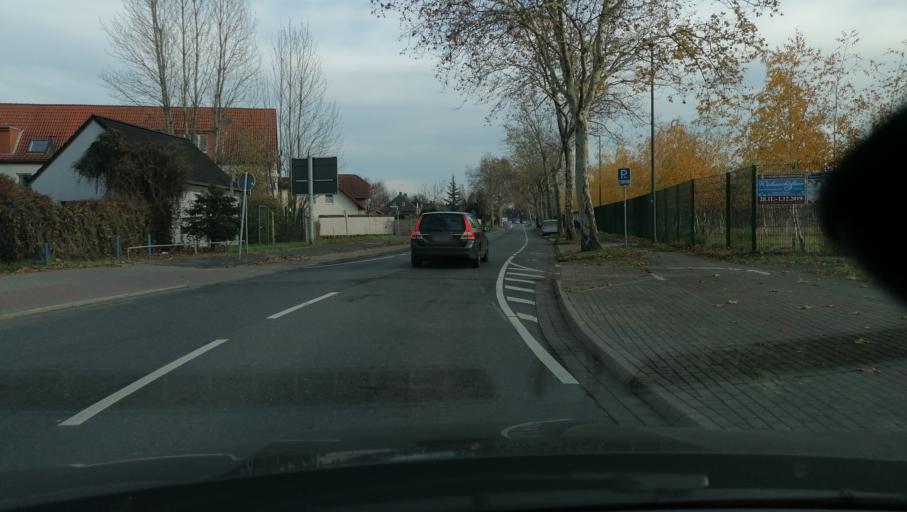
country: DE
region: North Rhine-Westphalia
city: Castrop-Rauxel
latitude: 51.5866
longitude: 7.3376
